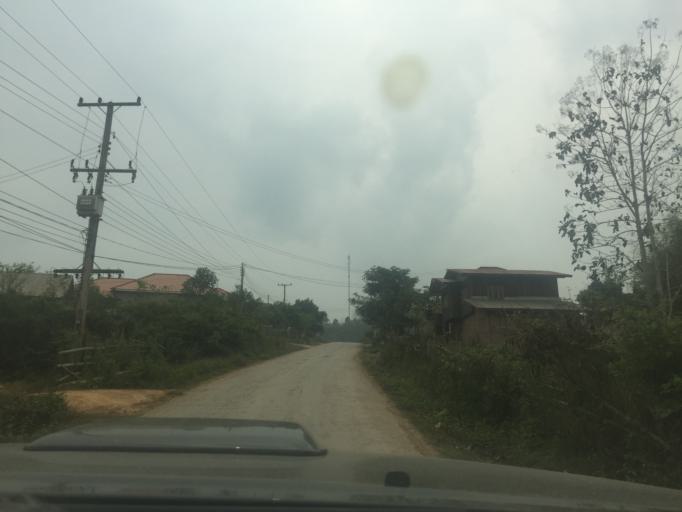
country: LA
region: Vientiane
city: Muang Sanakham
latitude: 18.4029
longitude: 101.5105
